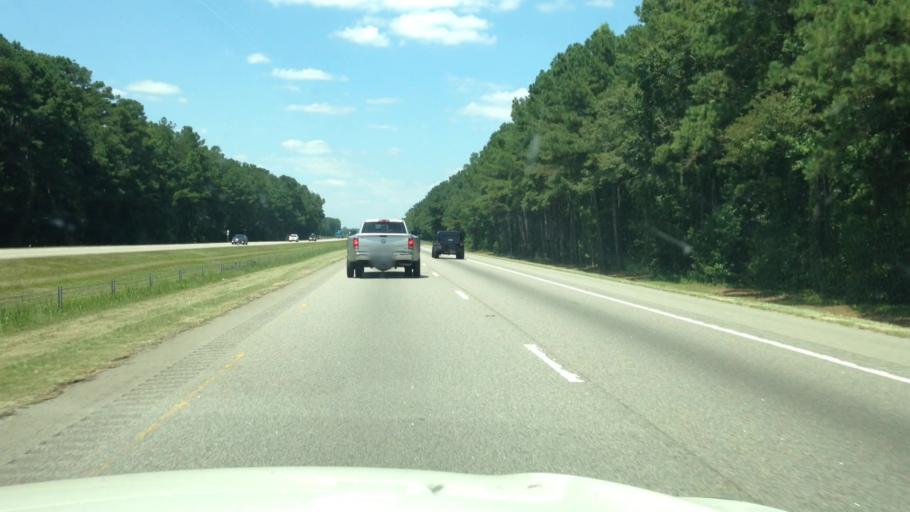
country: US
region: North Carolina
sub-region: Robeson County
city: Saint Pauls
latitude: 34.7769
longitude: -78.9956
